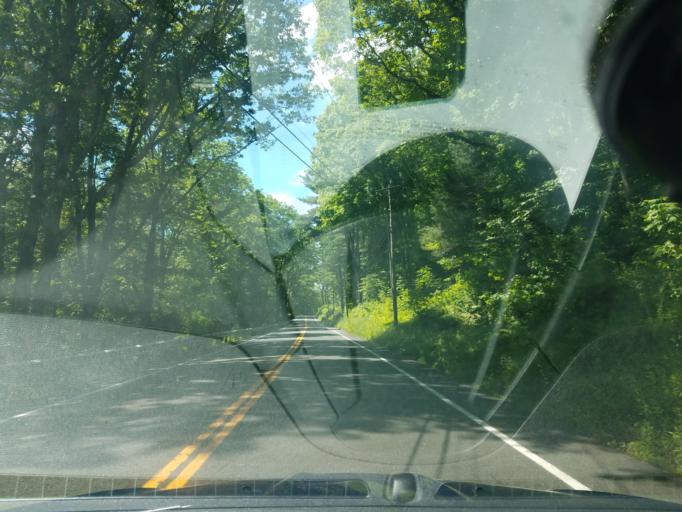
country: US
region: Massachusetts
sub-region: Berkshire County
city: New Marlborough
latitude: 42.0219
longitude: -73.2026
